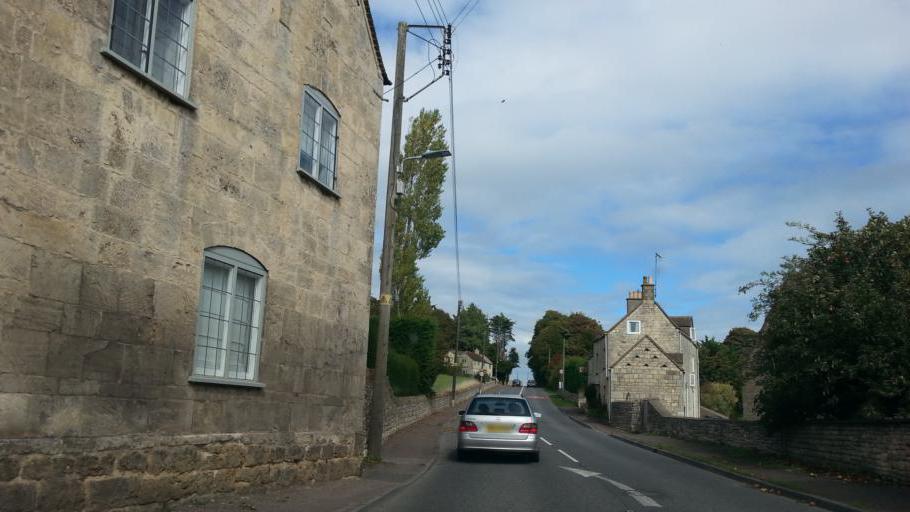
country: GB
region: England
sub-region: Gloucestershire
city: Painswick
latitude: 51.7898
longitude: -2.1915
